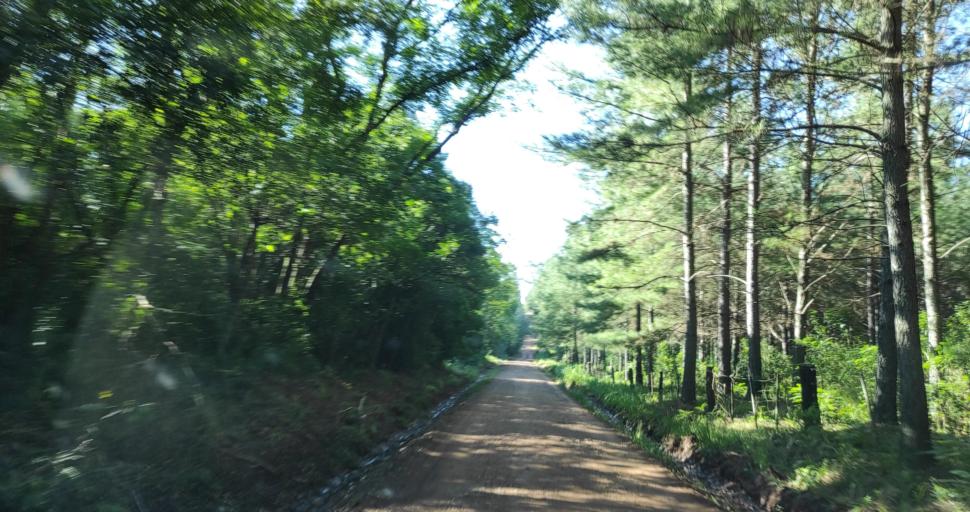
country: AR
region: Misiones
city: Capiovi
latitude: -26.9294
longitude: -55.0011
